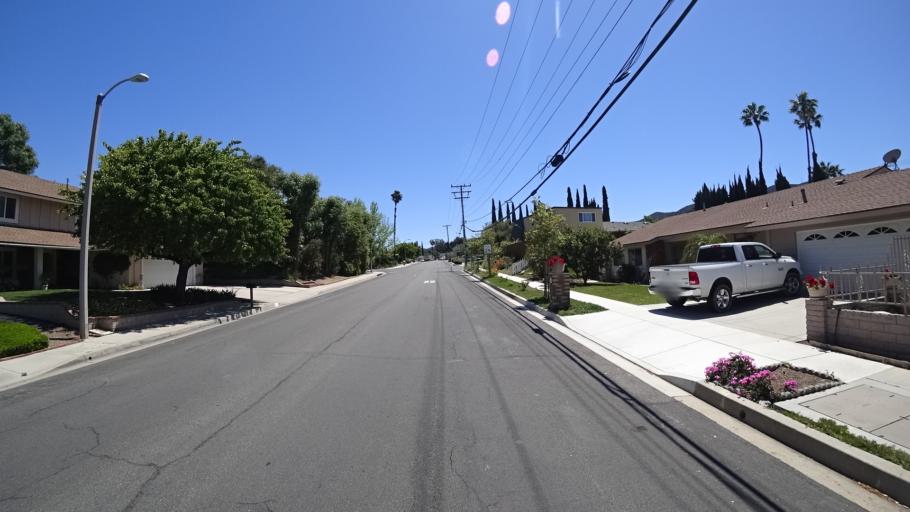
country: US
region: California
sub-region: Ventura County
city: Casa Conejo
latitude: 34.1829
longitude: -118.9033
